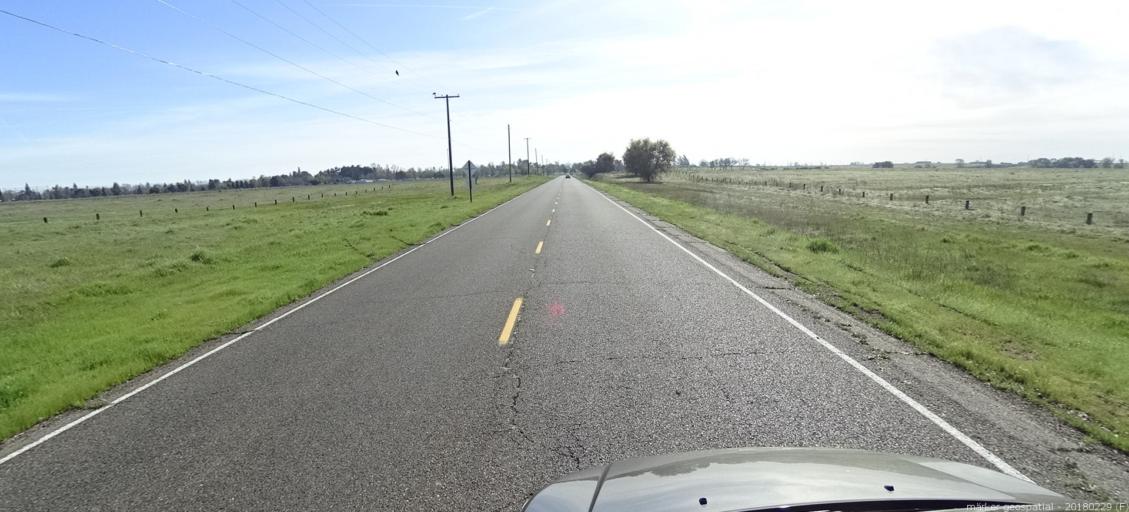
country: US
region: California
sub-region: Sacramento County
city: Rancho Cordova
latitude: 38.5466
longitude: -121.2676
